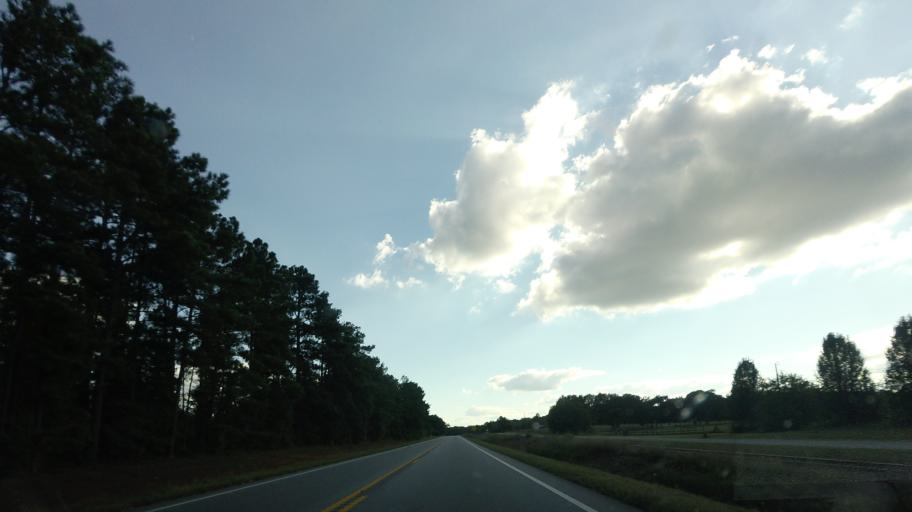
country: US
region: Georgia
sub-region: Lamar County
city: Barnesville
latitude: 33.0220
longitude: -84.1820
